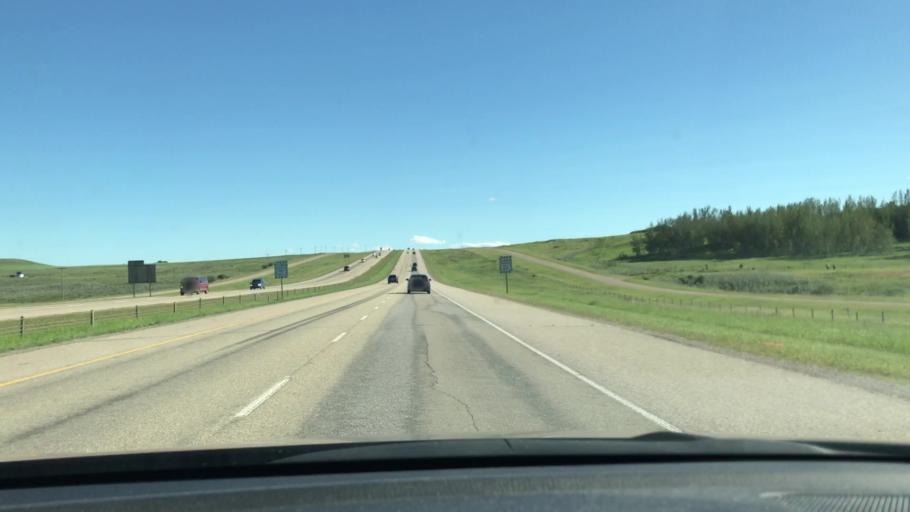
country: CA
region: Alberta
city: Carstairs
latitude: 51.5502
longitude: -114.0254
